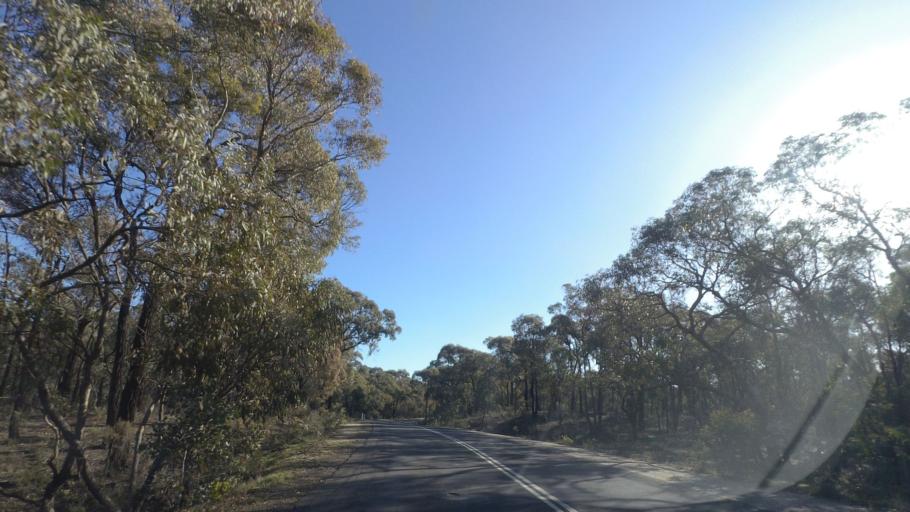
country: AU
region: Victoria
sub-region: Greater Bendigo
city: Kangaroo Flat
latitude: -36.8222
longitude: 144.2677
